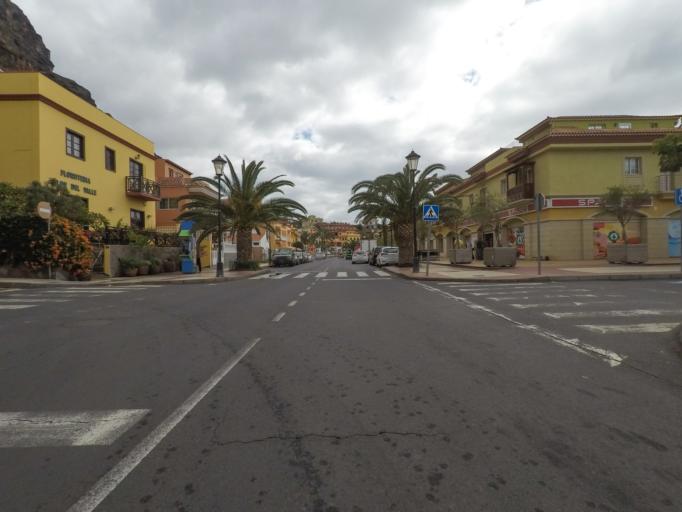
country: ES
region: Canary Islands
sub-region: Provincia de Santa Cruz de Tenerife
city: Alajero
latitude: 28.0863
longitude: -17.3347
